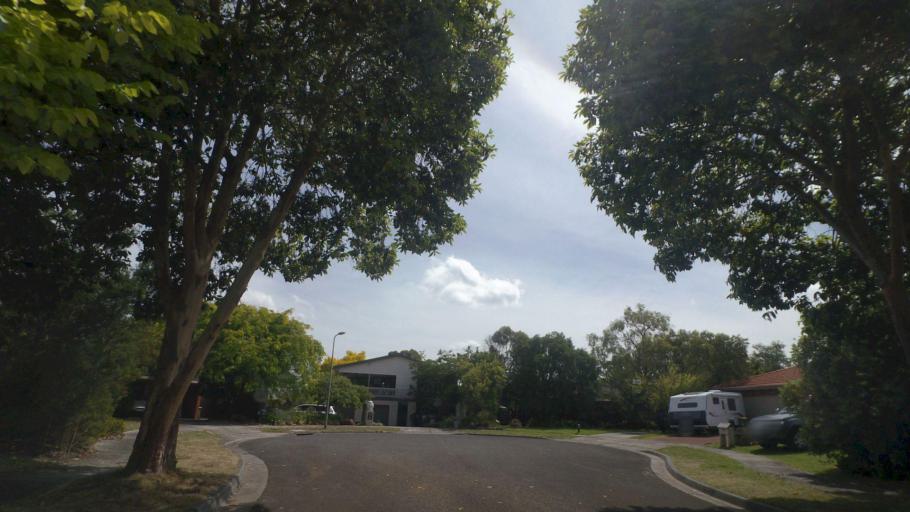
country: AU
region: Victoria
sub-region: Knox
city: The Basin
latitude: -37.8502
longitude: 145.3034
